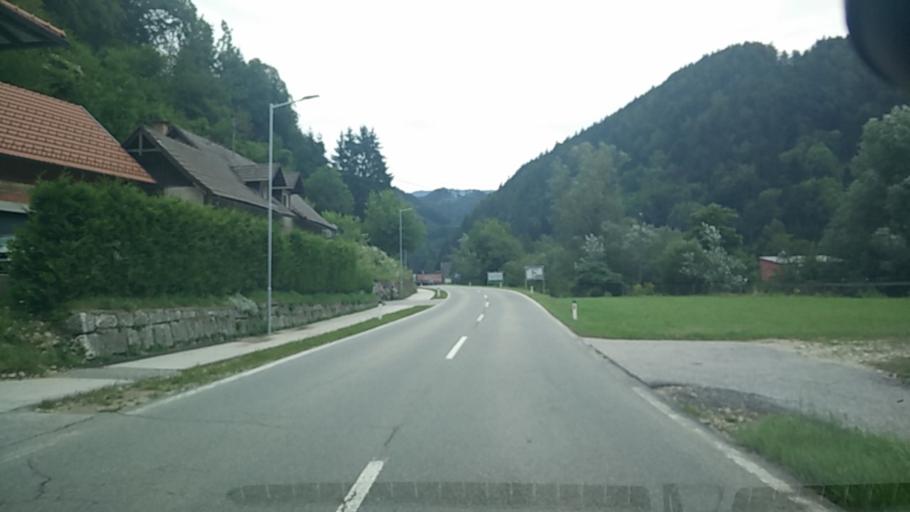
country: AT
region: Carinthia
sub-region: Politischer Bezirk Volkermarkt
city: Bad Eisenkappel
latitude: 46.4918
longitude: 14.5855
